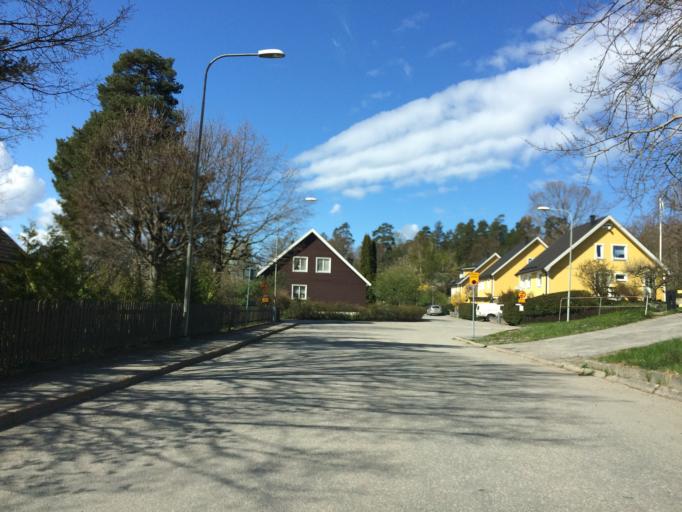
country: SE
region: Stockholm
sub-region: Huddinge Kommun
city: Segeltorp
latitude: 59.2877
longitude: 17.9035
